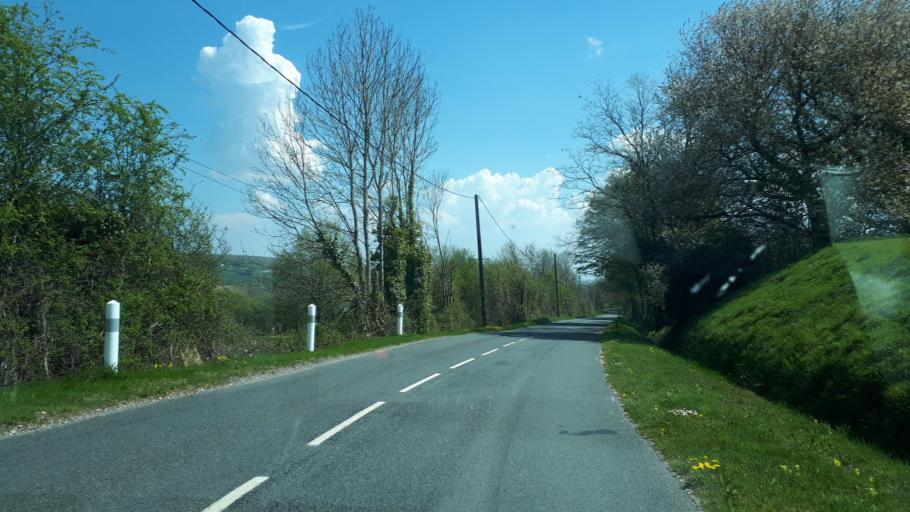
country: FR
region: Centre
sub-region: Departement du Cher
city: Henrichemont
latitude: 47.3049
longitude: 2.6221
